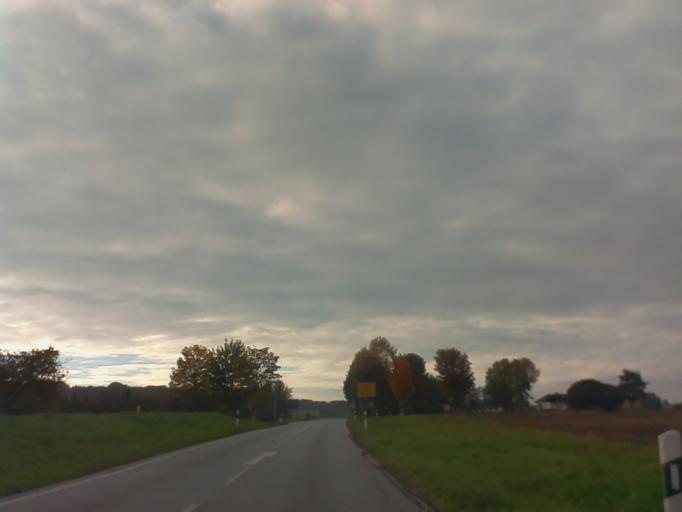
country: DE
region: Hesse
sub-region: Regierungsbezirk Darmstadt
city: Brensbach
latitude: 49.7751
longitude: 8.9410
